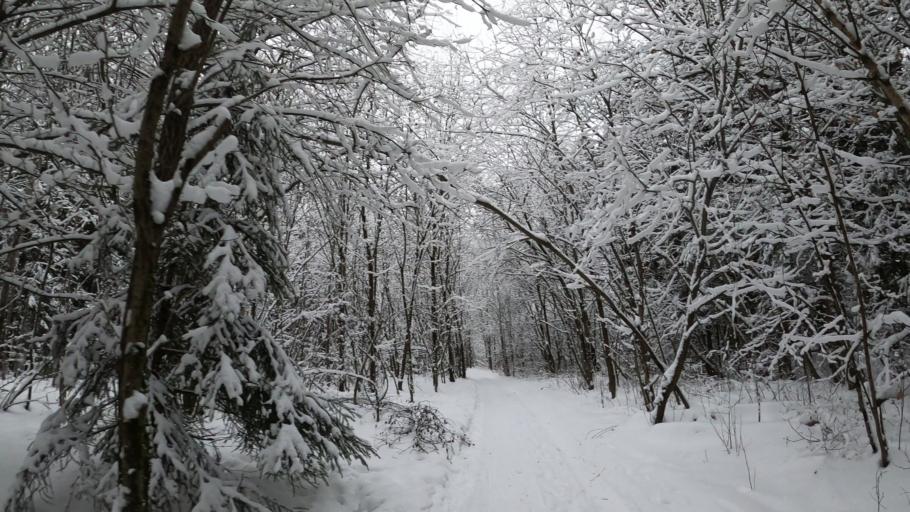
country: RU
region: Moskovskaya
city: Firsanovka
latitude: 55.9351
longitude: 37.2179
